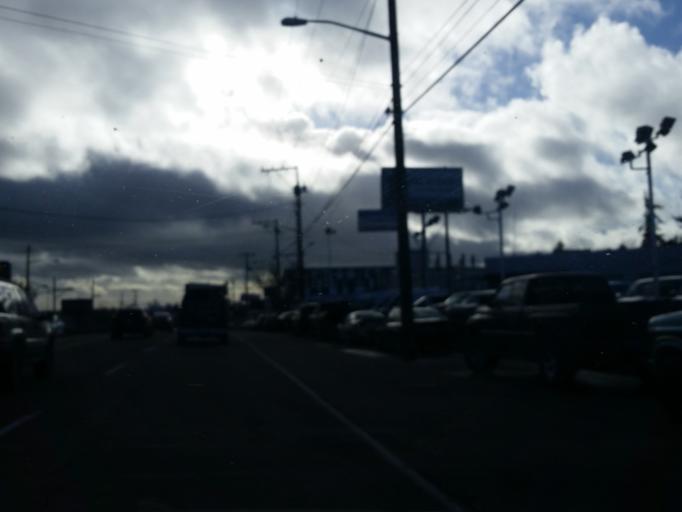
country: US
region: Washington
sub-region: King County
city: Shoreline
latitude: 47.7296
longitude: -122.3452
